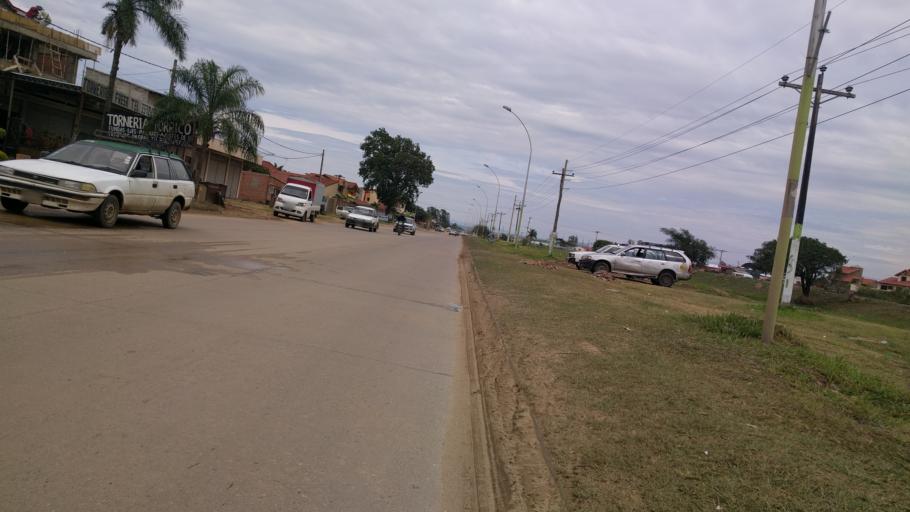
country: BO
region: Santa Cruz
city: Santa Cruz de la Sierra
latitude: -17.8447
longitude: -63.1745
